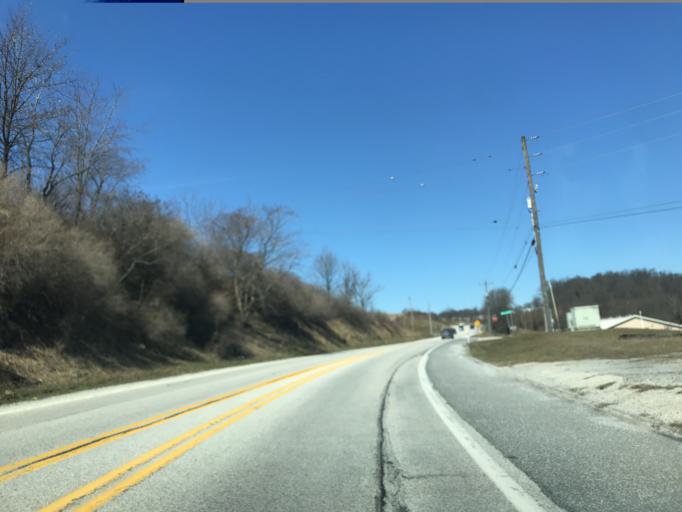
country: US
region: Pennsylvania
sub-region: York County
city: Shrewsbury
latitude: 39.7647
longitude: -76.6520
